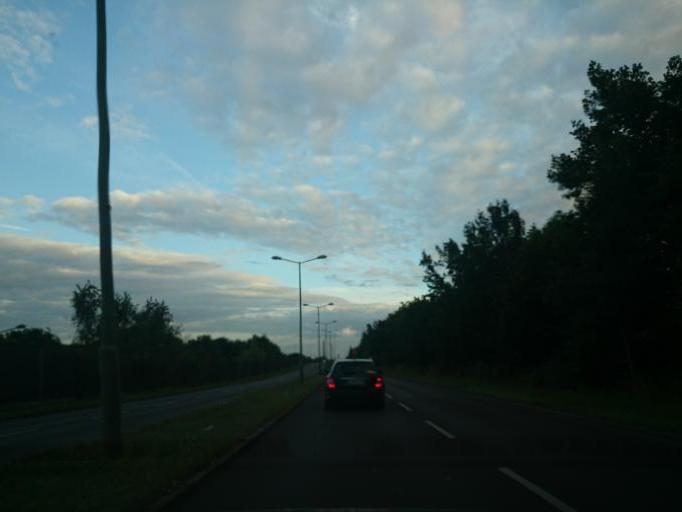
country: DE
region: Berlin
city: Kopenick Bezirk
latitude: 52.4525
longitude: 13.5584
